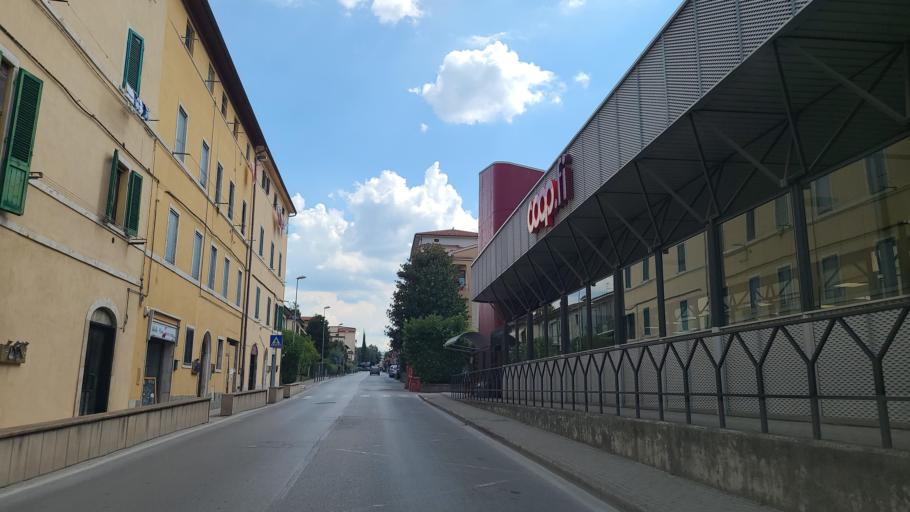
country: IT
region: Tuscany
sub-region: Provincia di Siena
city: Colle di Val d'Elsa
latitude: 43.4193
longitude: 11.1280
